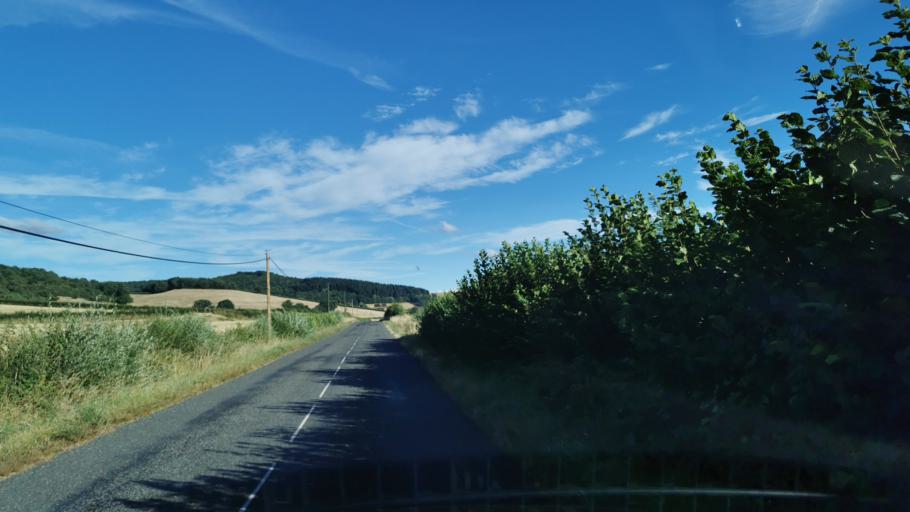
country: FR
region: Bourgogne
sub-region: Departement de Saone-et-Loire
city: Marmagne
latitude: 46.8210
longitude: 4.3243
